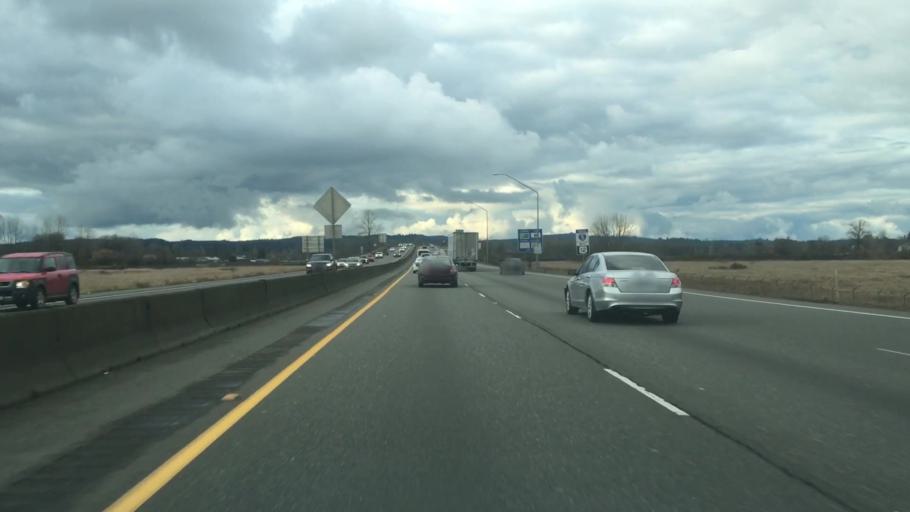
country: US
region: Washington
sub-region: Lewis County
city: Chehalis
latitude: 46.6478
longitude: -122.9648
